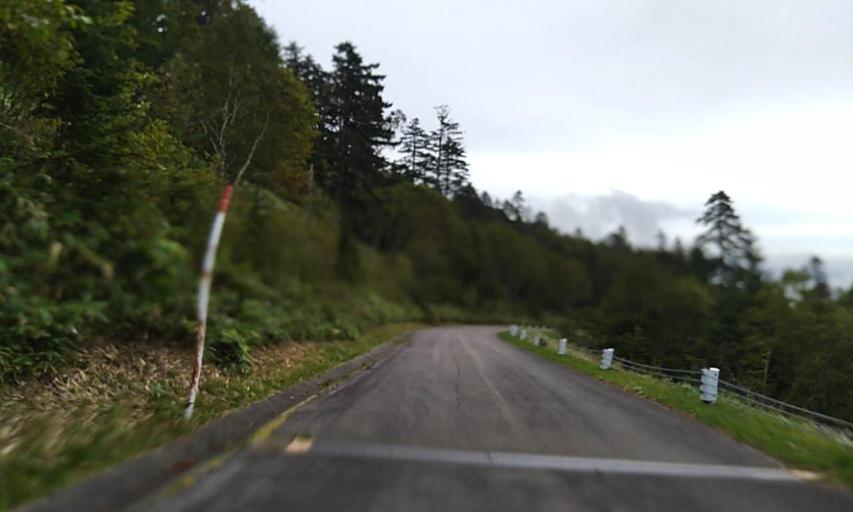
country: JP
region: Hokkaido
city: Bihoro
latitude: 43.5662
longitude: 144.2233
